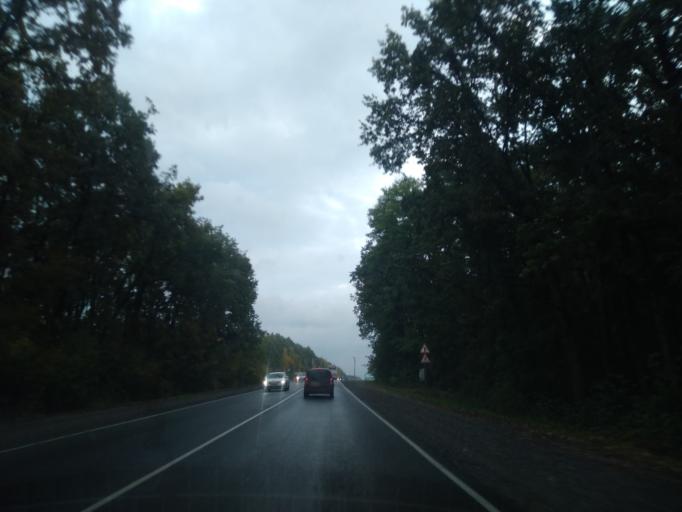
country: RU
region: Lipetsk
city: Borinskoye
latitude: 52.5938
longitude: 39.2698
